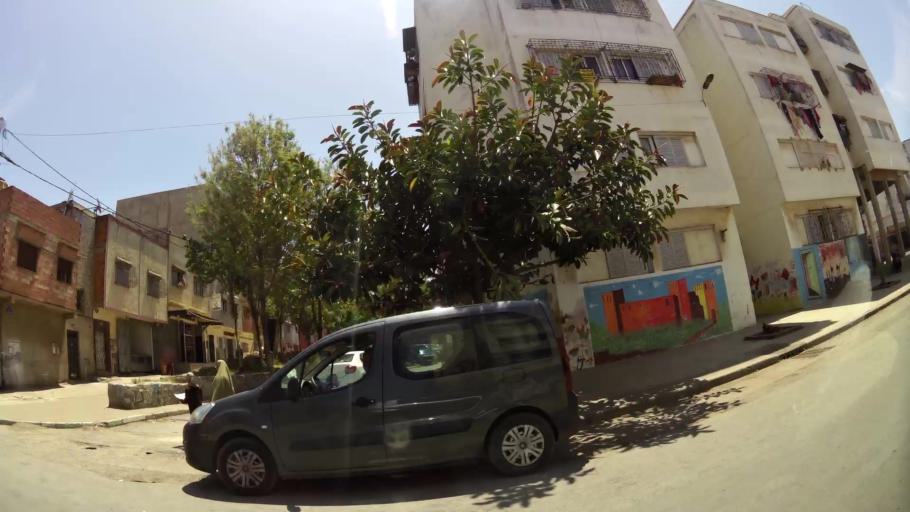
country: MA
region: Rabat-Sale-Zemmour-Zaer
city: Sale
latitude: 34.0690
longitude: -6.7856
